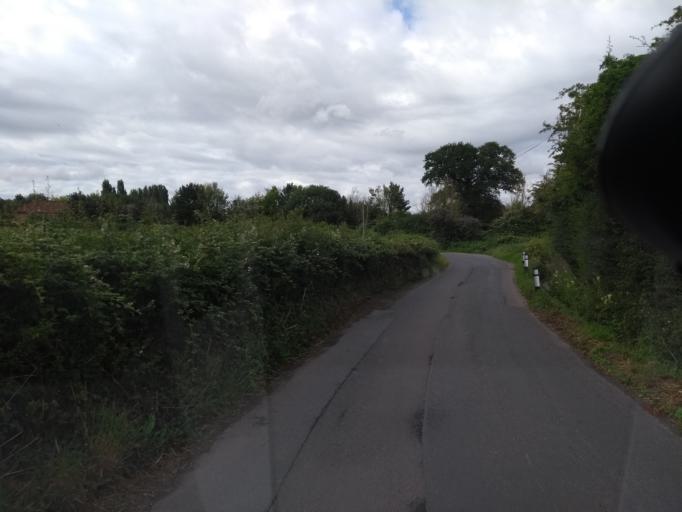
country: GB
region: England
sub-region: Somerset
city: Bridgwater
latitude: 51.1086
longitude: -2.9842
